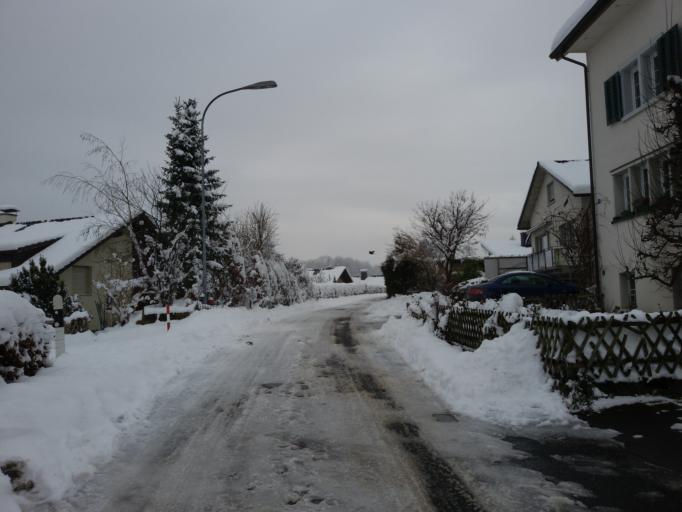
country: CH
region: Zurich
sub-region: Bezirk Hinwil
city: Rueti / Westlicher Dorfteil
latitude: 47.2564
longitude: 8.8416
